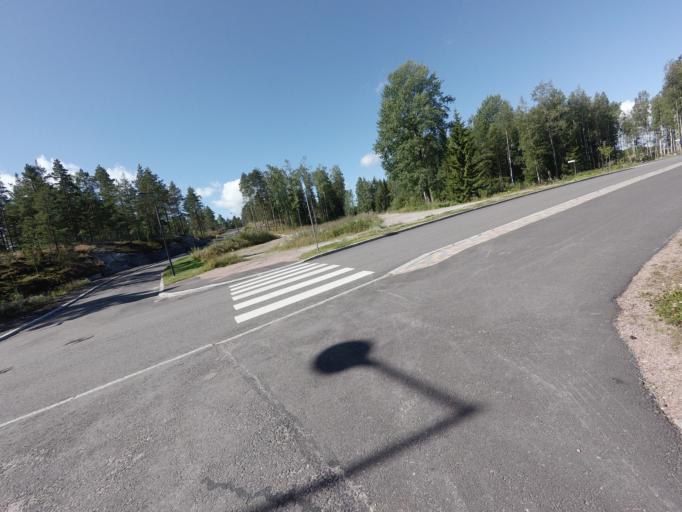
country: FI
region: Uusimaa
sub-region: Helsinki
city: Espoo
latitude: 60.1465
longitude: 24.5871
